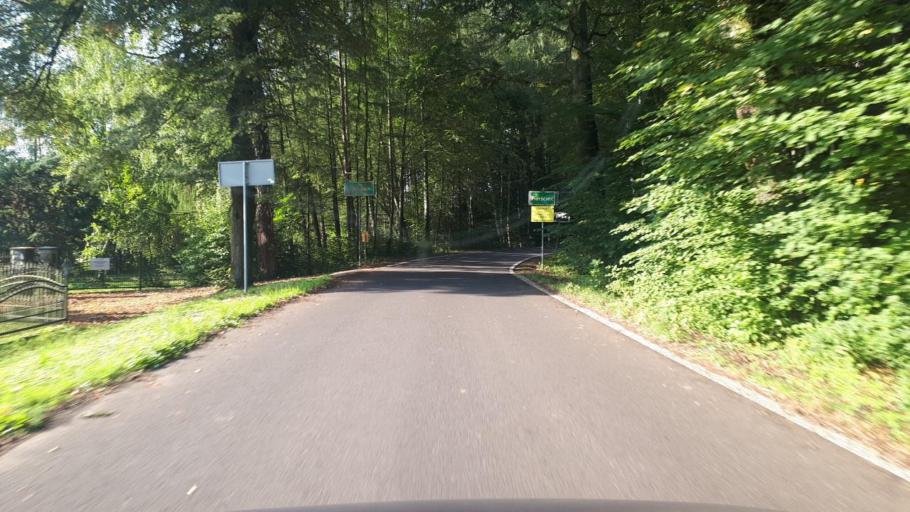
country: PL
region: Silesian Voivodeship
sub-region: Powiat cieszynski
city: Piersciec
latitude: 49.8520
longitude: 18.8398
